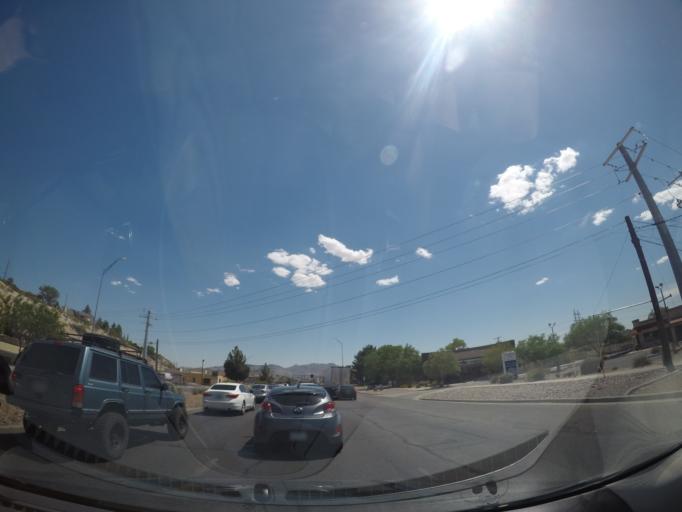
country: US
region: Texas
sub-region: El Paso County
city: El Paso
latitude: 31.8002
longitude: -106.5107
